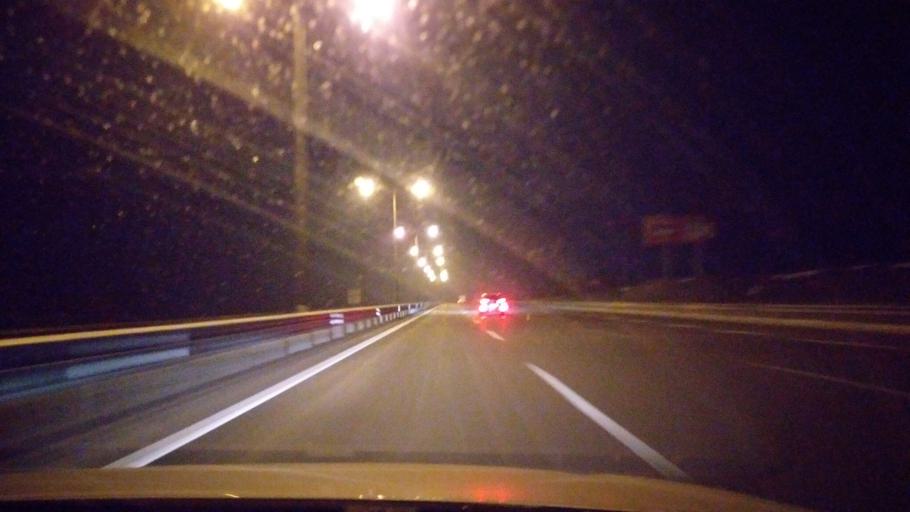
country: TR
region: Bolu
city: Dortdivan
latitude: 40.7539
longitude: 32.0734
